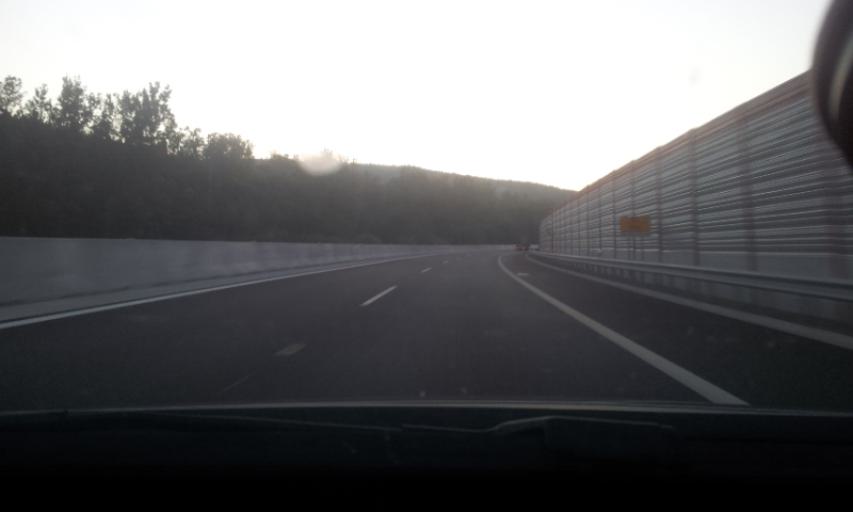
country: SK
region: Banskobystricky
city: Detva
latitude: 48.5368
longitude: 19.4320
